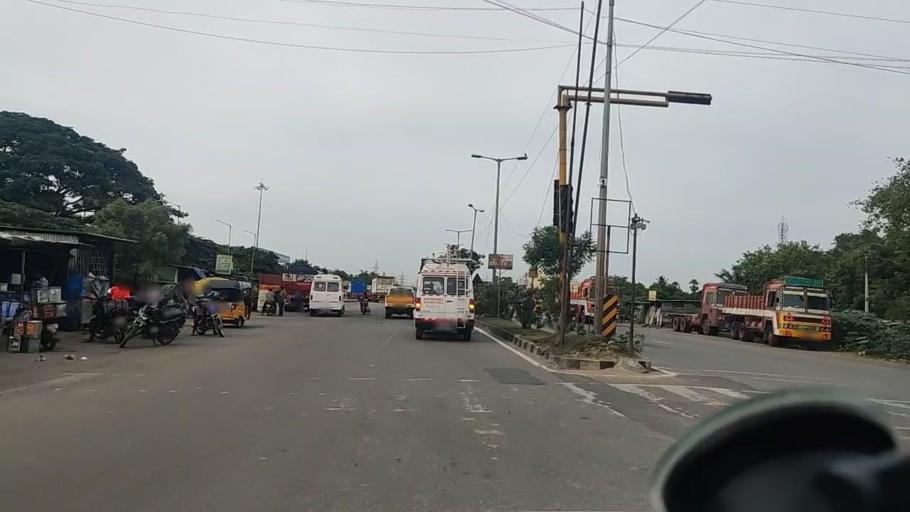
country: IN
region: Tamil Nadu
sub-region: Thiruvallur
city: Chinnasekkadu
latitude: 13.1634
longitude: 80.2278
